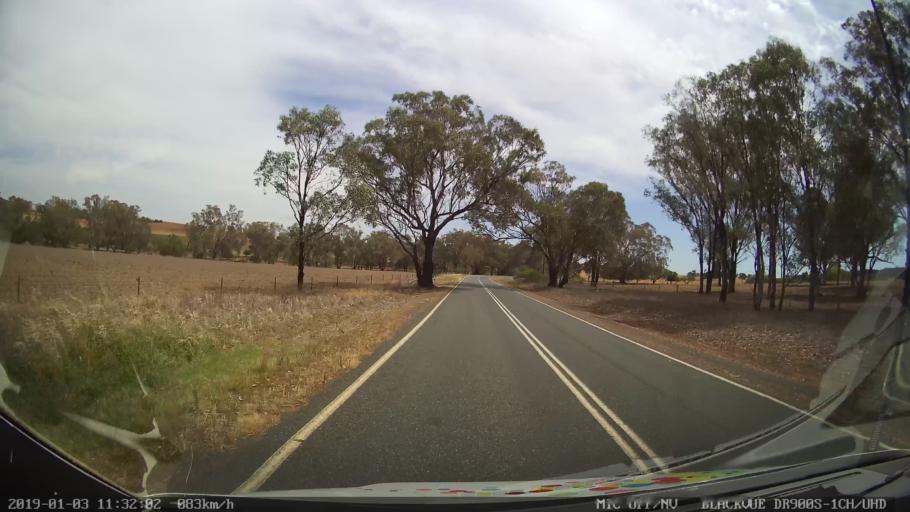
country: AU
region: New South Wales
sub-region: Weddin
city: Grenfell
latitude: -33.9633
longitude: 148.1806
